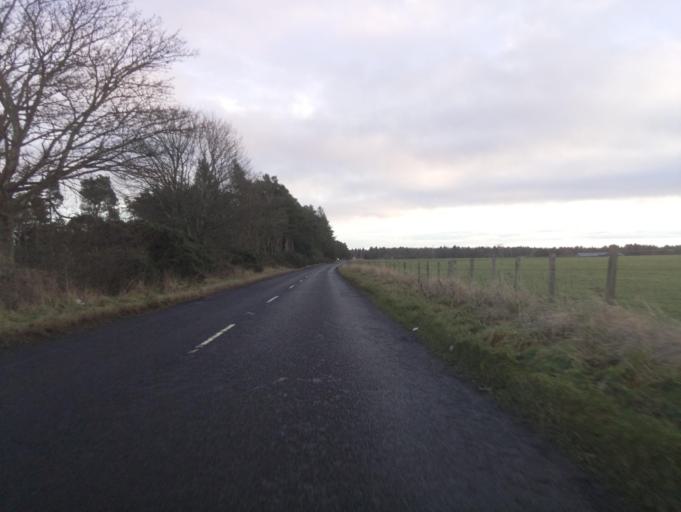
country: GB
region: Scotland
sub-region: Angus
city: Letham
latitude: 56.5572
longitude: -2.7661
